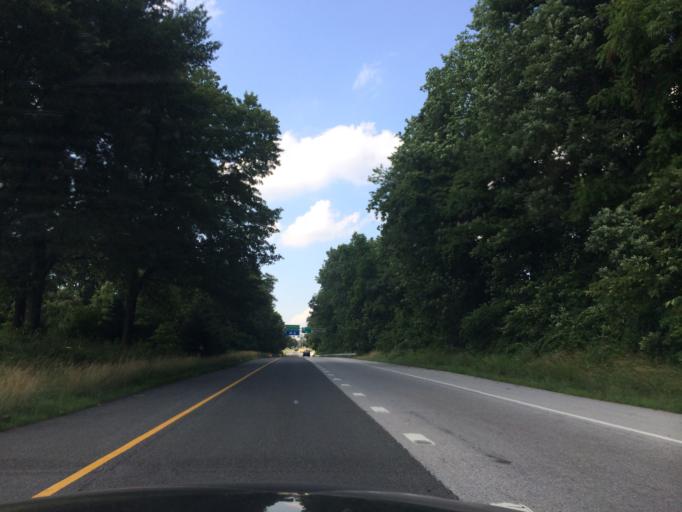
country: US
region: Maryland
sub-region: Howard County
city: Ellicott City
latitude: 39.2727
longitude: -76.8176
